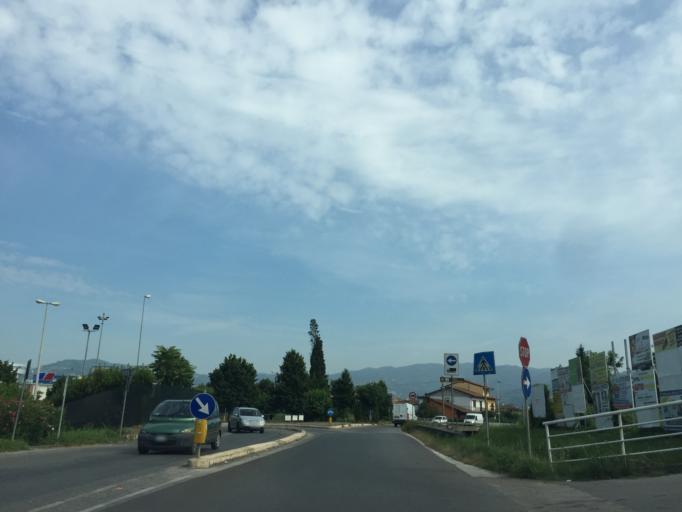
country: IT
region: Tuscany
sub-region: Provincia di Pistoia
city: Margine Coperta-Traversagna
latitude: 43.8623
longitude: 10.7668
